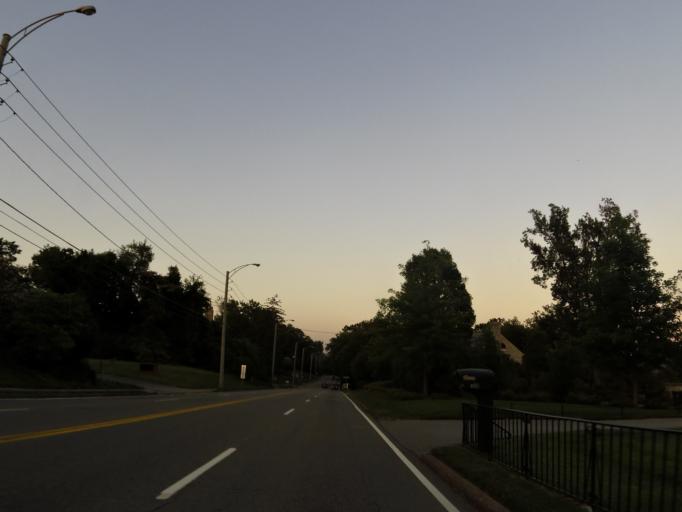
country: US
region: Tennessee
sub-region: Knox County
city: Knoxville
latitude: 35.9508
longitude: -83.9535
